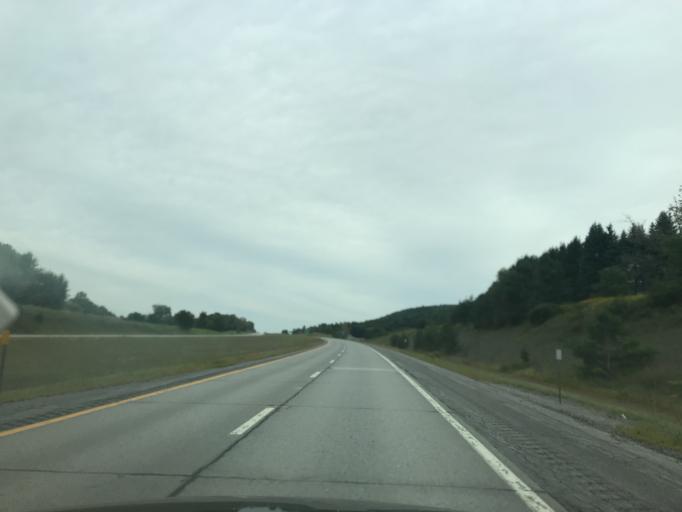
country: US
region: New York
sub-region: Schoharie County
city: Cobleskill
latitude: 42.6726
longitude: -74.4512
